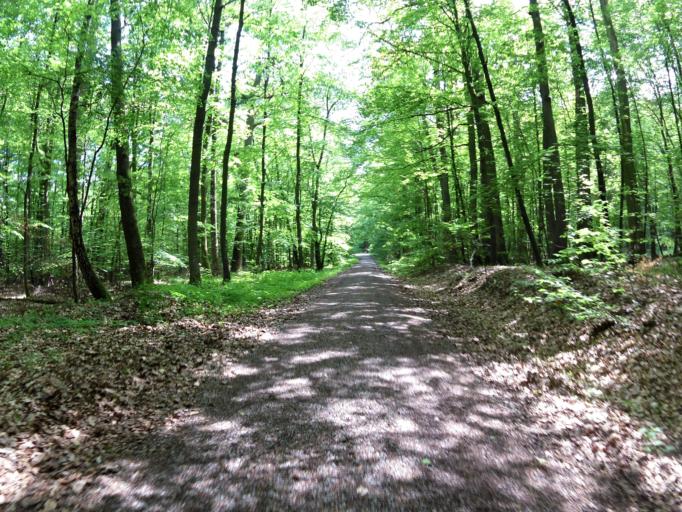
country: DE
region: Bavaria
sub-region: Regierungsbezirk Unterfranken
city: Kist
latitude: 49.7332
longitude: 9.8604
